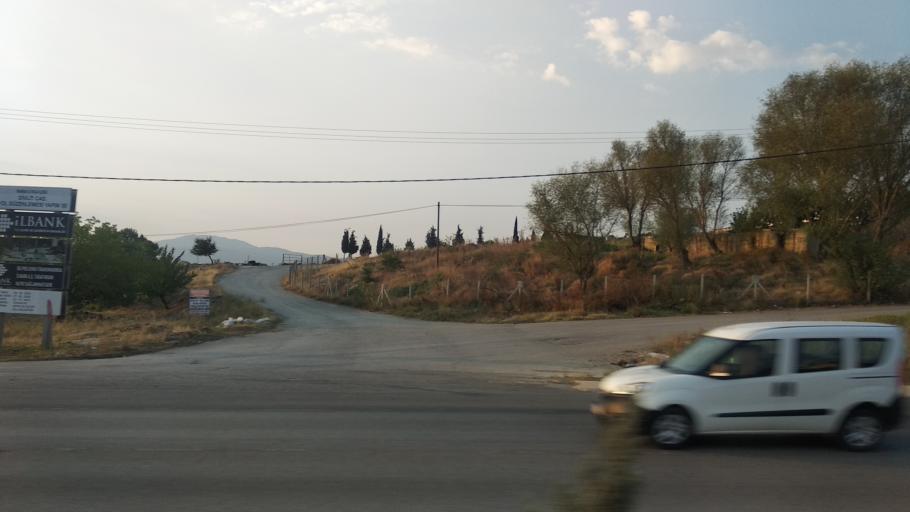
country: TR
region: Manisa
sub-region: Kula
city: Kula
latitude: 38.5483
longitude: 28.6731
